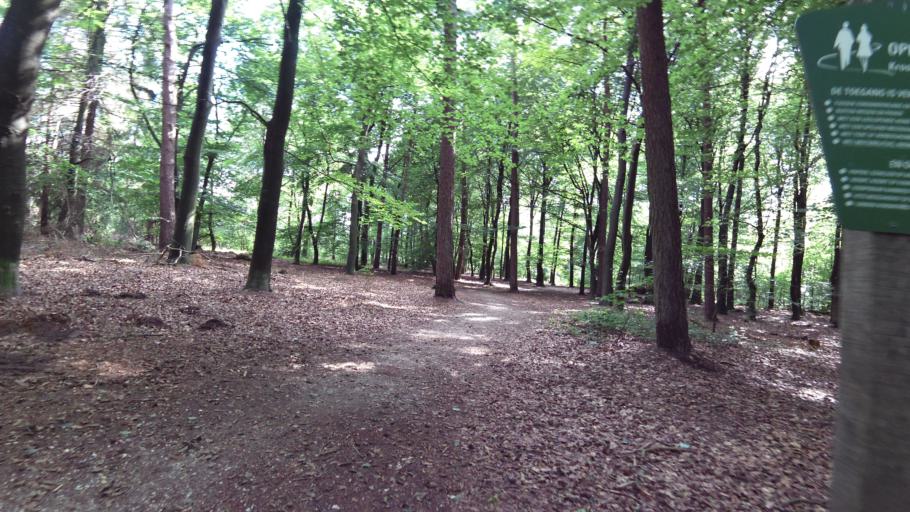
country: NL
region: Gelderland
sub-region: Gemeente Epe
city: Vaassen
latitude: 52.2790
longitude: 5.9220
